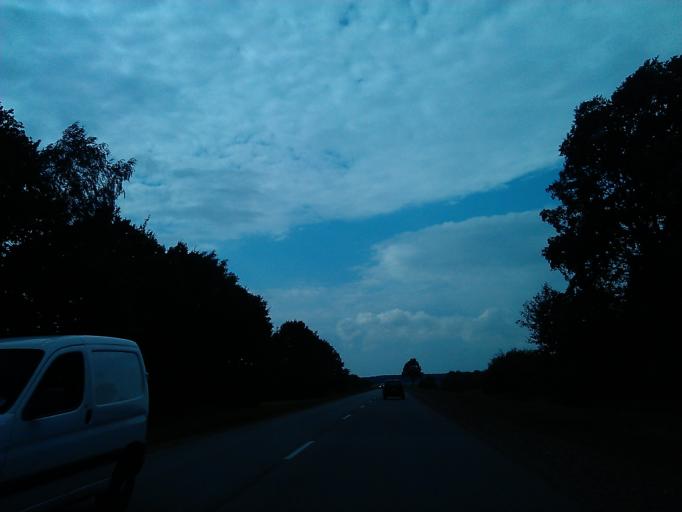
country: LV
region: Rundales
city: Pilsrundale
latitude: 56.4048
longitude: 24.0946
